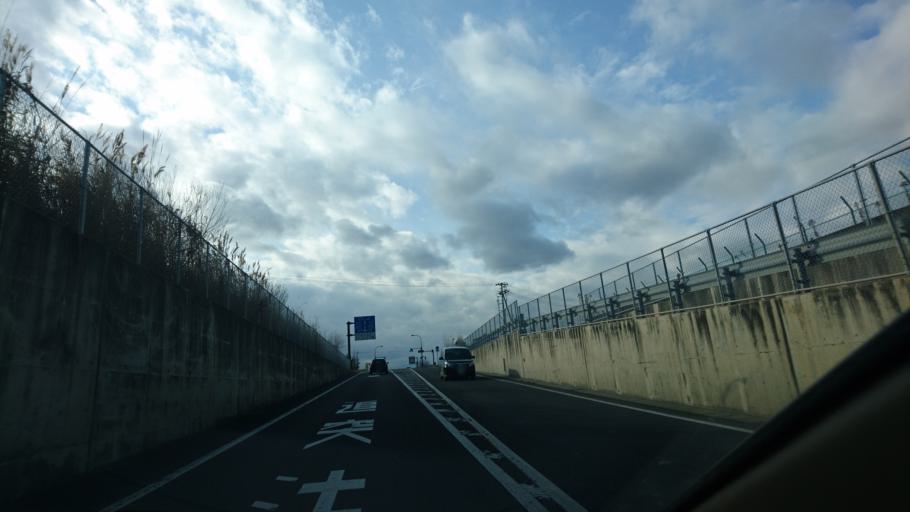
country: JP
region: Miyagi
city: Kogota
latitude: 38.5542
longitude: 141.0626
